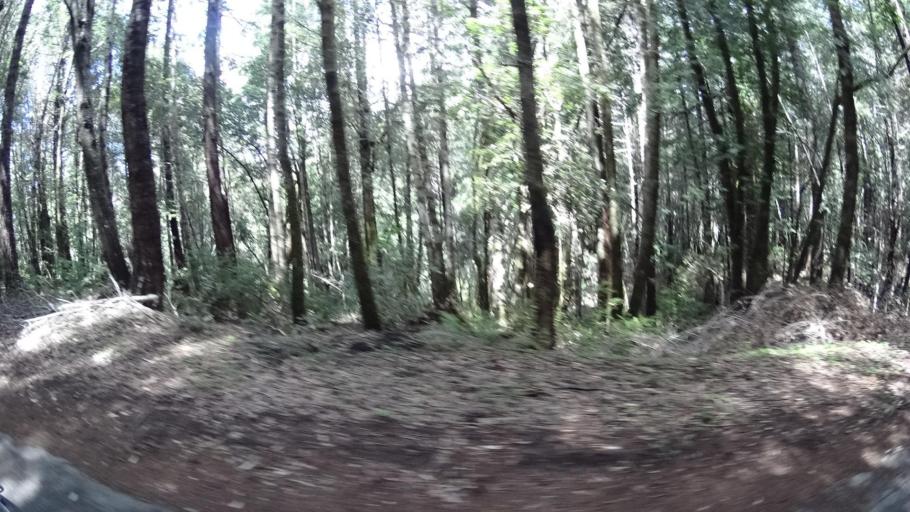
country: US
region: California
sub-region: Humboldt County
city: Blue Lake
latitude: 40.7591
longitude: -123.9693
